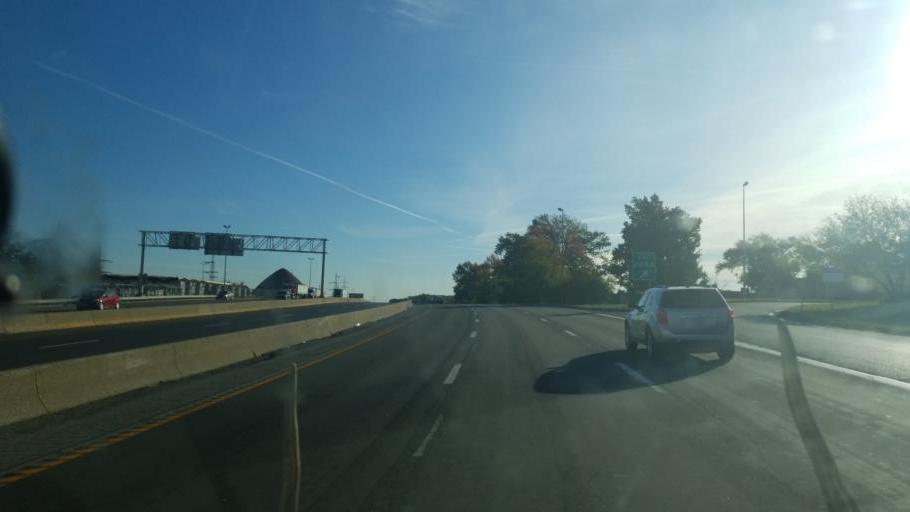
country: US
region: Missouri
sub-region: Saint Louis County
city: Pine Lawn
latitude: 38.6827
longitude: -90.2379
